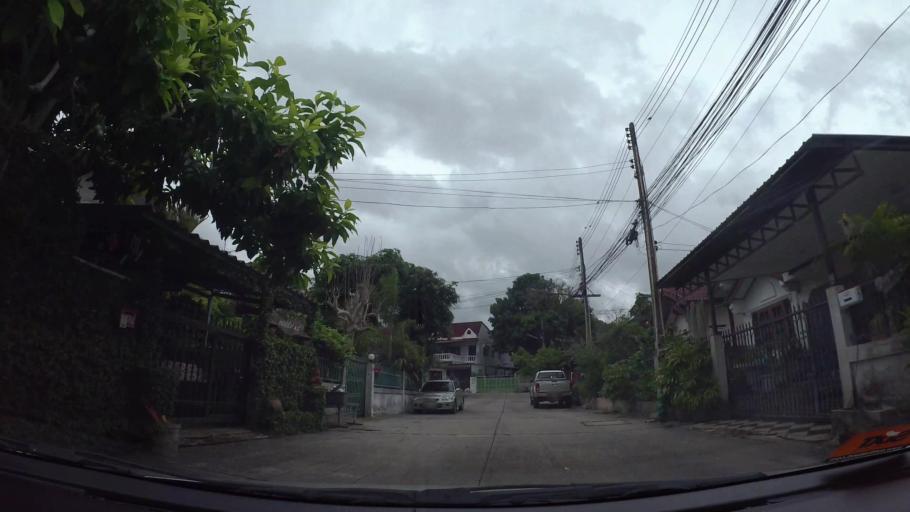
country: TH
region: Chon Buri
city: Si Racha
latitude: 13.2044
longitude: 100.9483
